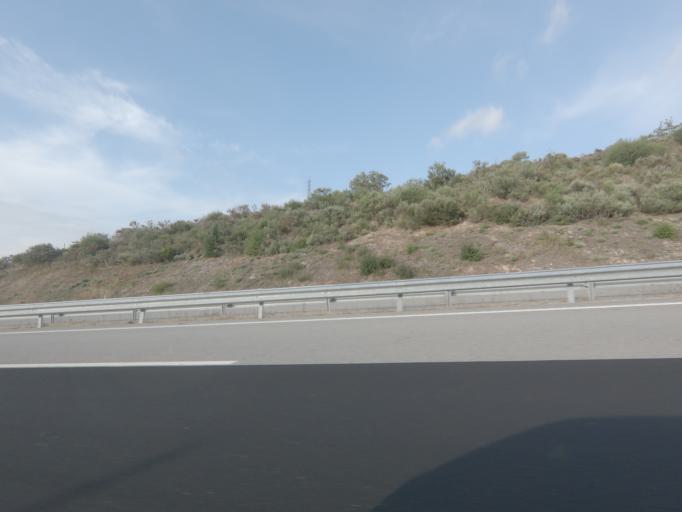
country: PT
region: Vila Real
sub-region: Vila Pouca de Aguiar
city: Vila Pouca de Aguiar
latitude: 41.4748
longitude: -7.6442
